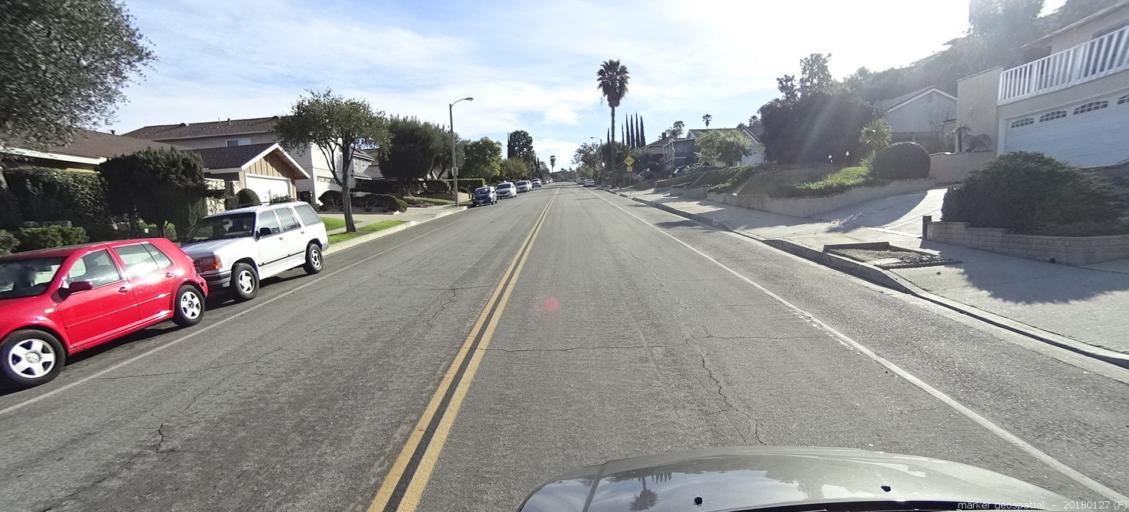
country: US
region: California
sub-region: Los Angeles County
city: Diamond Bar
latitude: 34.0337
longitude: -117.8027
